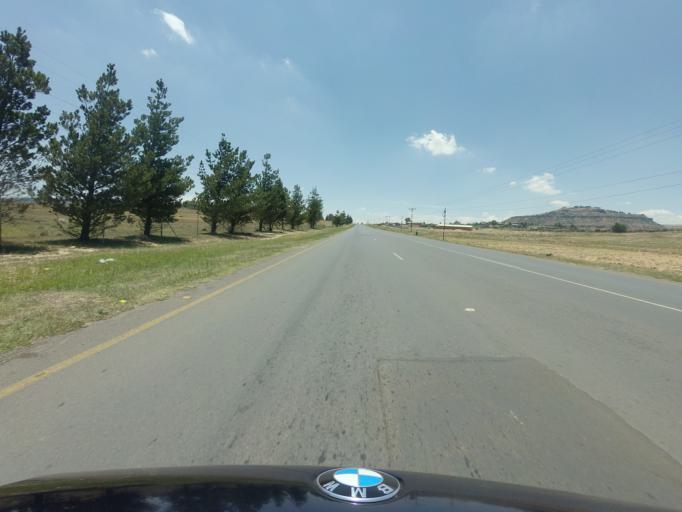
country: LS
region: Maseru
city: Maseru
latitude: -29.2647
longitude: 27.5554
